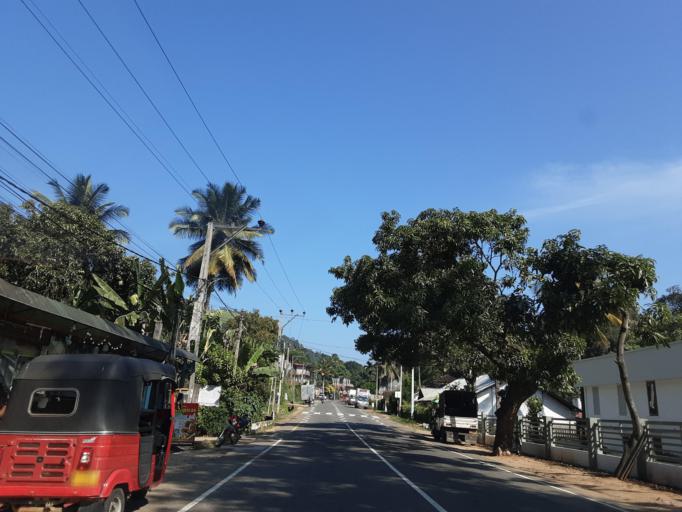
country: LK
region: Uva
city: Badulla
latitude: 6.9988
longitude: 81.0569
